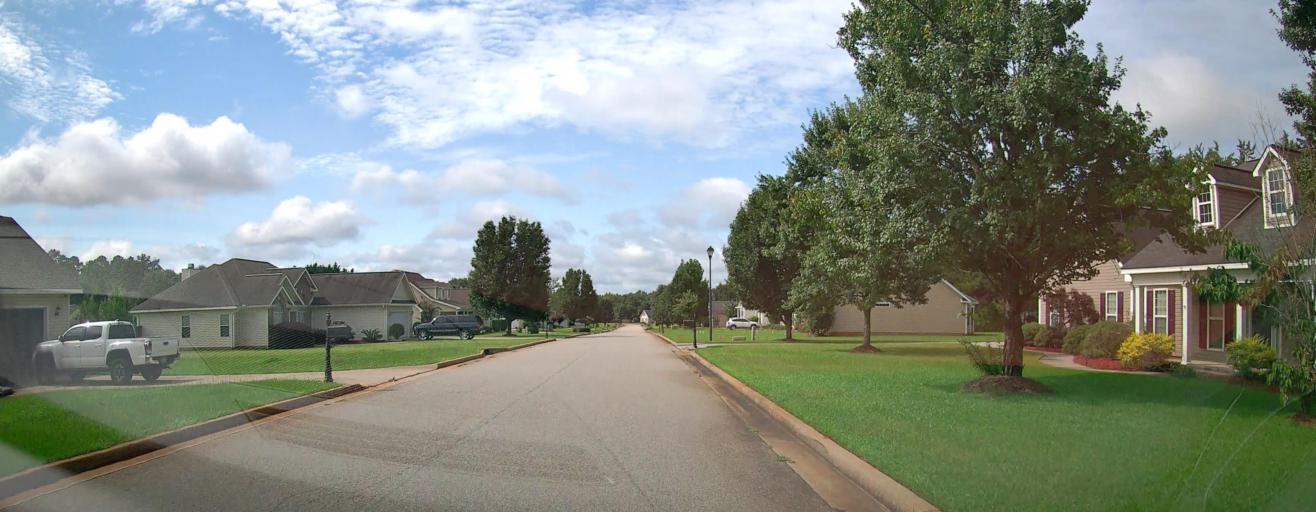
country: US
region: Georgia
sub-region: Peach County
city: Byron
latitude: 32.6488
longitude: -83.7257
